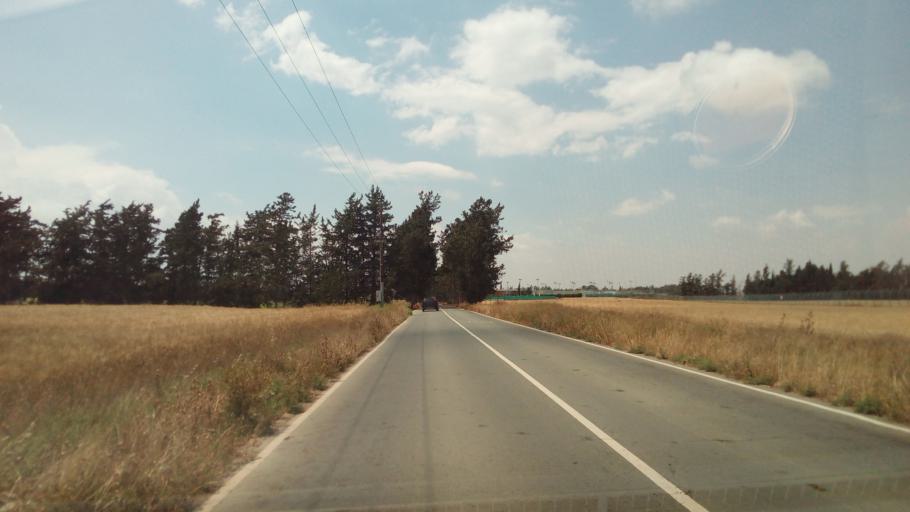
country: CY
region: Larnaka
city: Meneou
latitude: 34.8529
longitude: 33.6070
